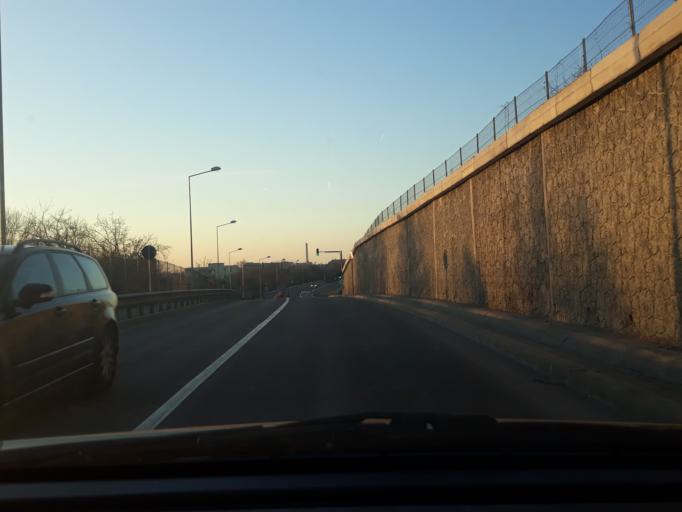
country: RO
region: Bihor
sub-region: Comuna Biharea
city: Oradea
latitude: 47.0605
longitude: 21.9452
